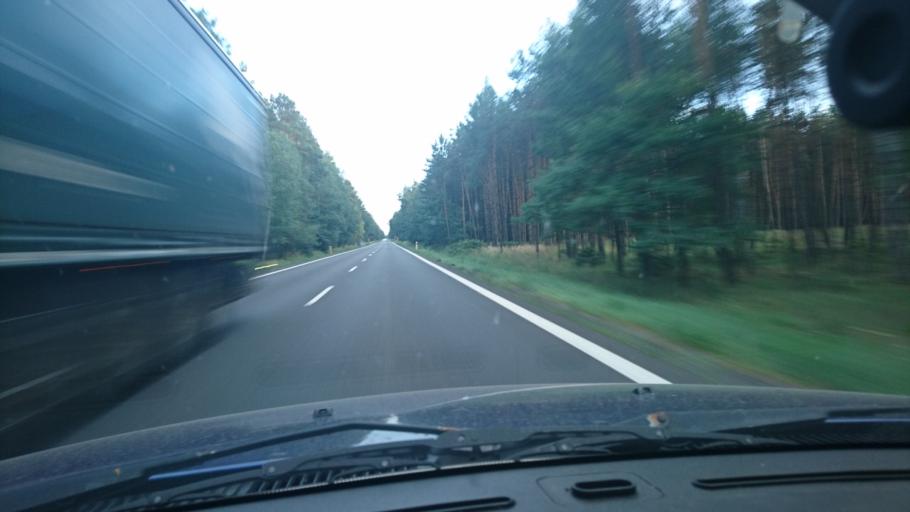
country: PL
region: Silesian Voivodeship
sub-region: Powiat tarnogorski
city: Tworog
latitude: 50.5726
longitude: 18.7103
